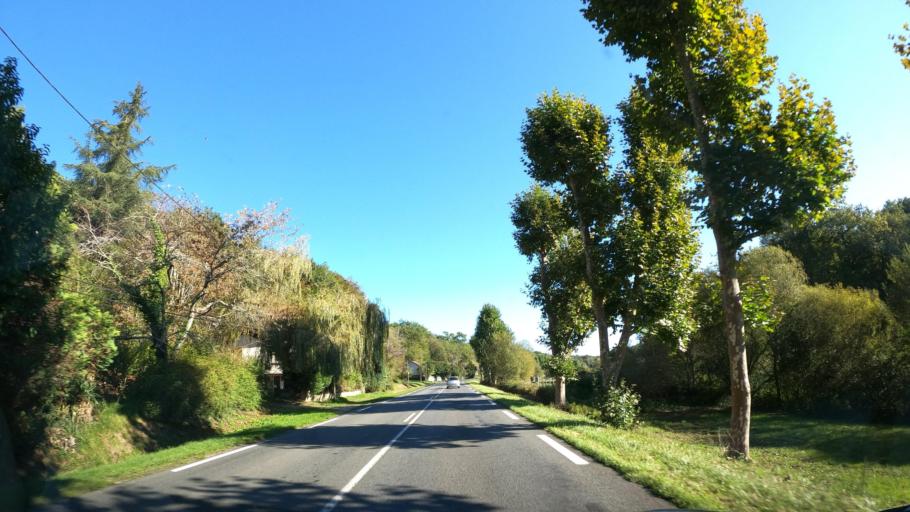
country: FR
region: Aquitaine
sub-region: Departement de la Dordogne
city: Lembras
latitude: 44.9436
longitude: 0.5697
